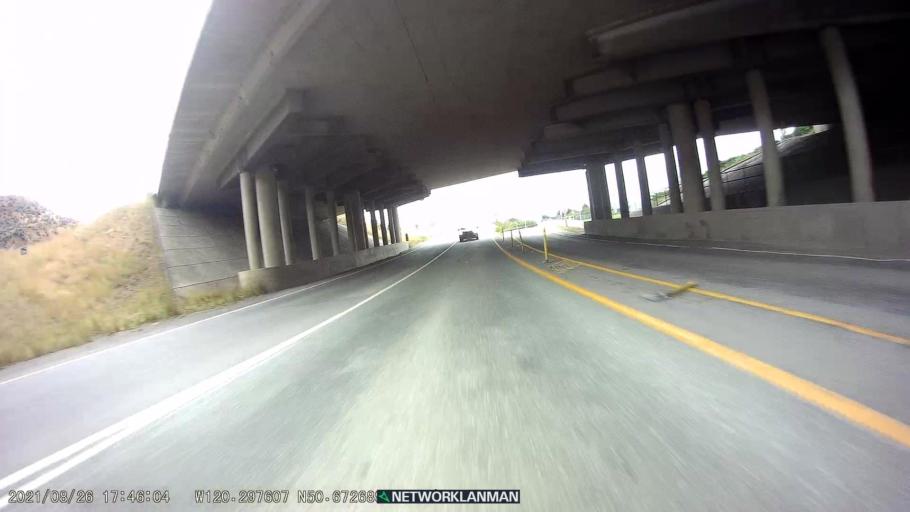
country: CA
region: British Columbia
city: Kamloops
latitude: 50.6724
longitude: -120.2968
